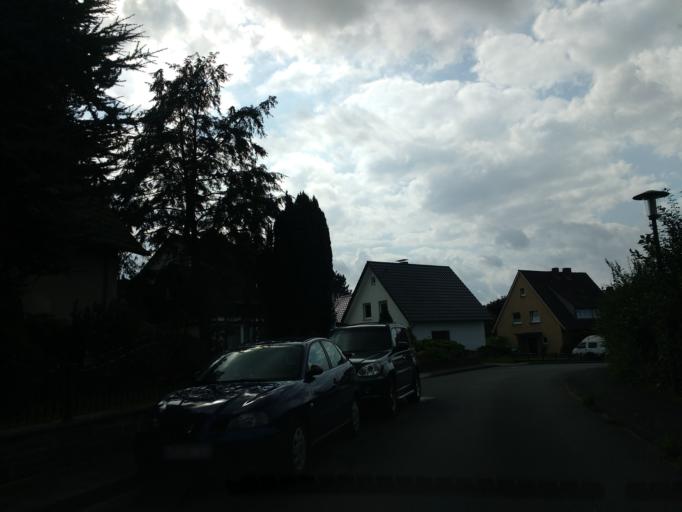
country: DE
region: North Rhine-Westphalia
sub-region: Regierungsbezirk Detmold
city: Lemgo
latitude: 52.0071
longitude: 8.8873
